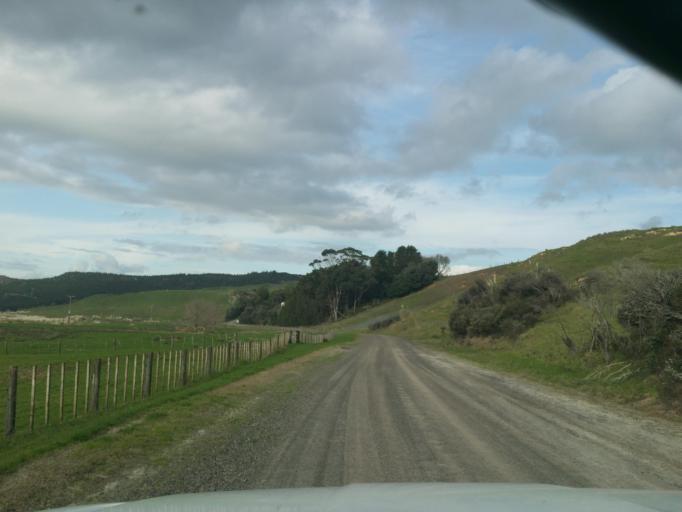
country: NZ
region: Northland
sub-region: Kaipara District
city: Dargaville
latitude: -35.8635
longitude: 173.7217
